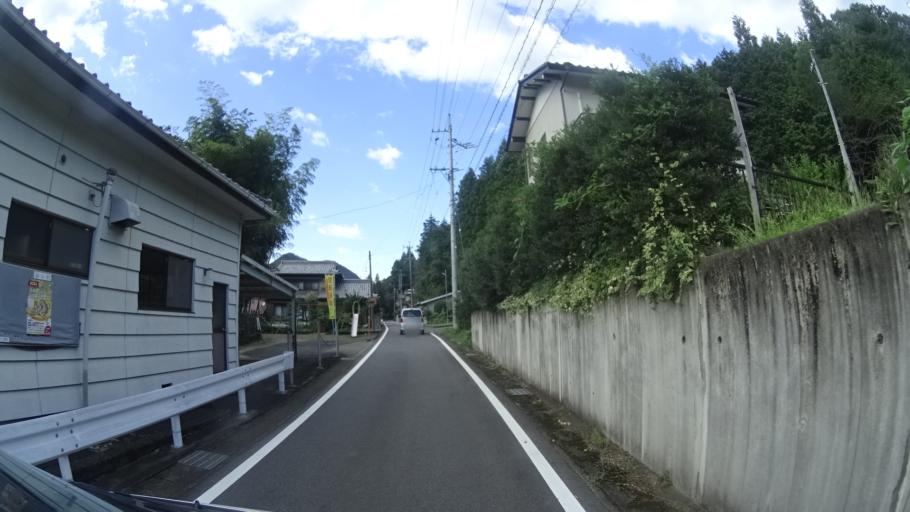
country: JP
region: Gifu
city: Minokamo
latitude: 35.5284
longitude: 137.1164
